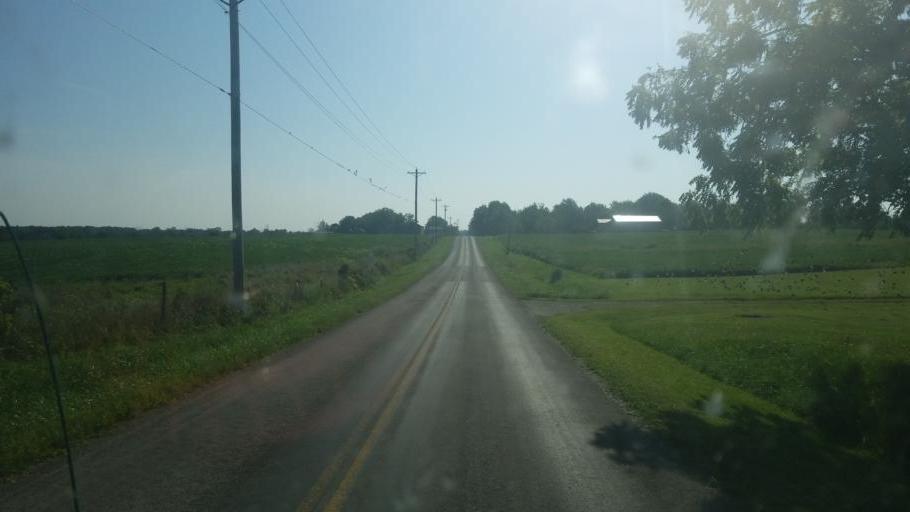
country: US
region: Ohio
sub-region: Huron County
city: New London
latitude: 41.0578
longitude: -82.2868
